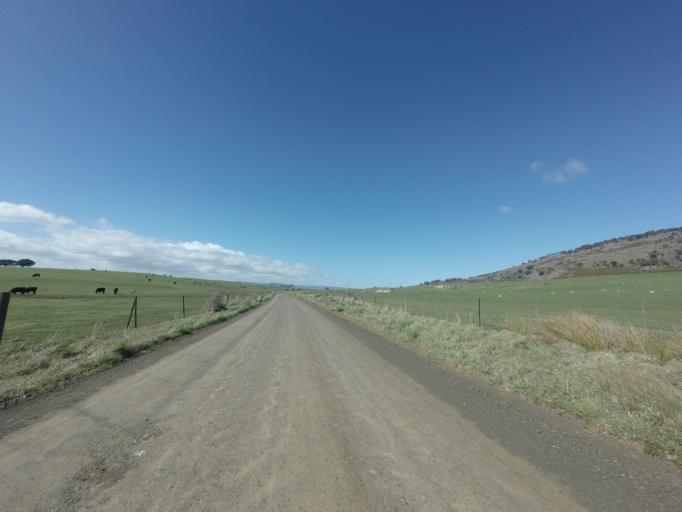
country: AU
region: Tasmania
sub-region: Northern Midlands
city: Evandale
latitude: -41.9183
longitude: 147.3922
